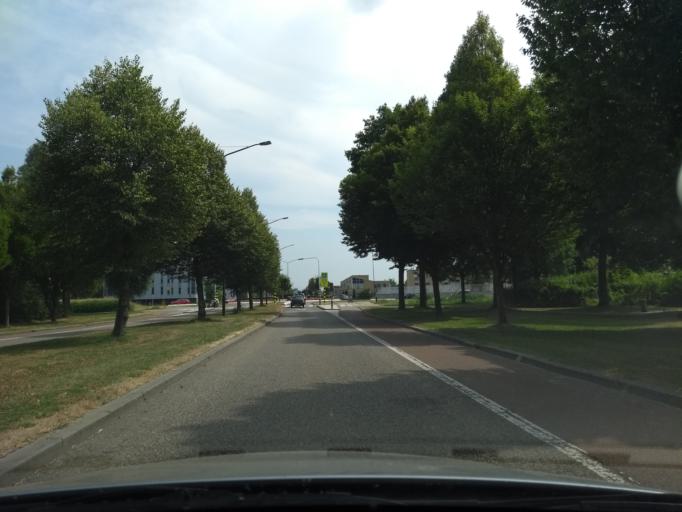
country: NL
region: North Holland
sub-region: Gemeente Heerhugowaard
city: Heerhugowaard
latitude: 52.6541
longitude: 4.8322
